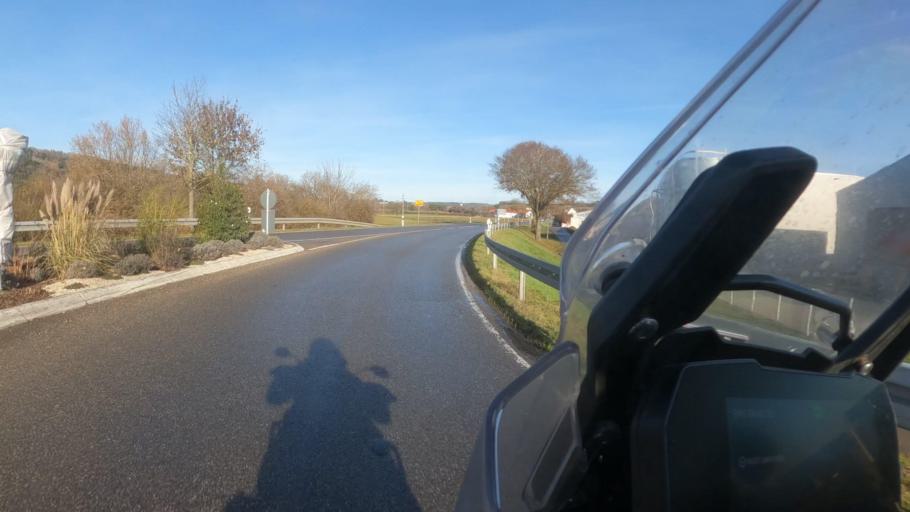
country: DE
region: Baden-Wuerttemberg
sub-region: Freiburg Region
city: Neuhausen
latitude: 47.8286
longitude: 8.7666
